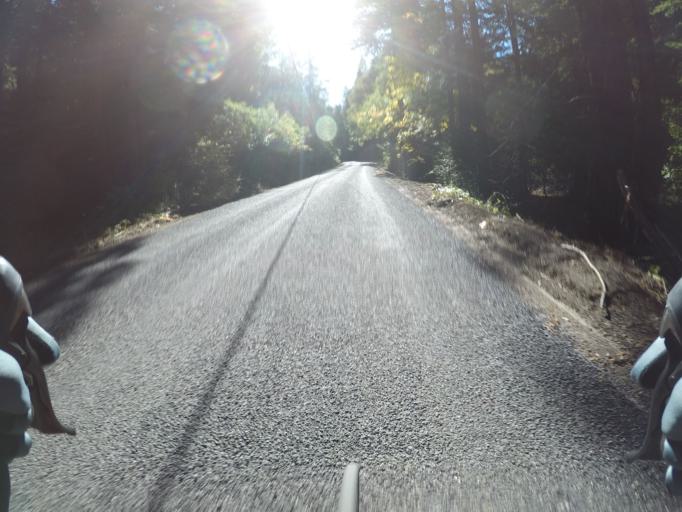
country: US
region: California
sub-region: Santa Cruz County
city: Lompico
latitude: 37.1123
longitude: -122.0206
